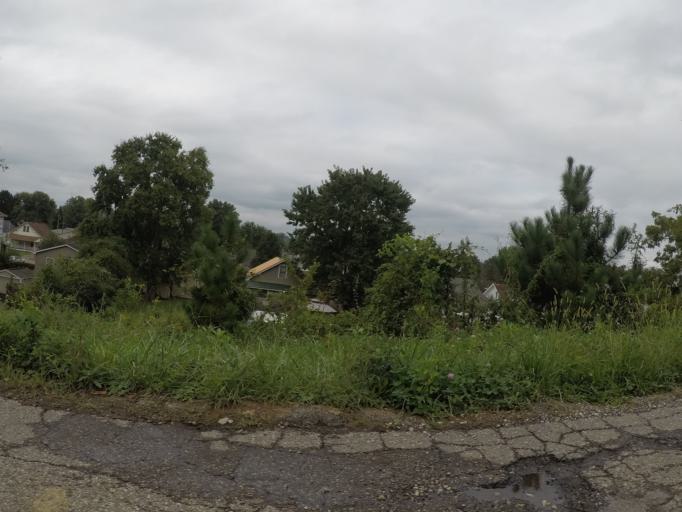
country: US
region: West Virginia
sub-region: Cabell County
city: Pea Ridge
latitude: 38.4283
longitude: -82.3750
